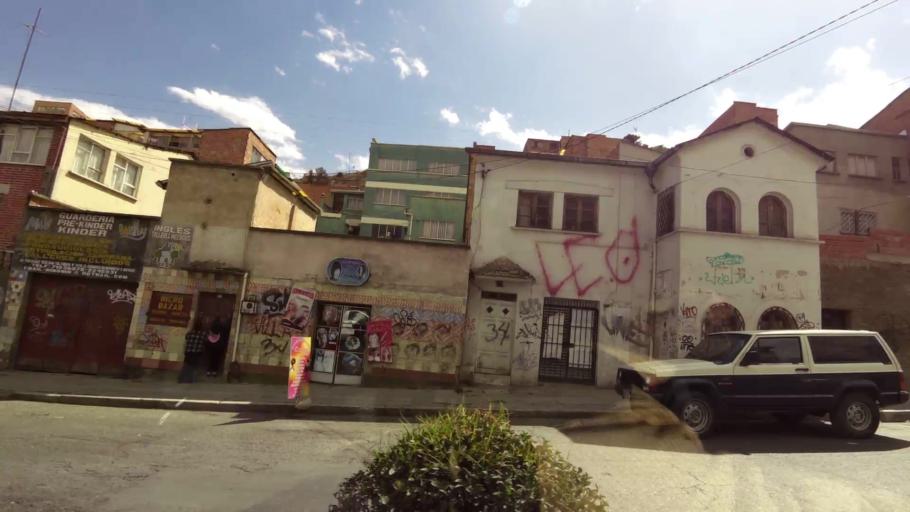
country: BO
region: La Paz
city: La Paz
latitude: -16.4955
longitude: -68.1259
